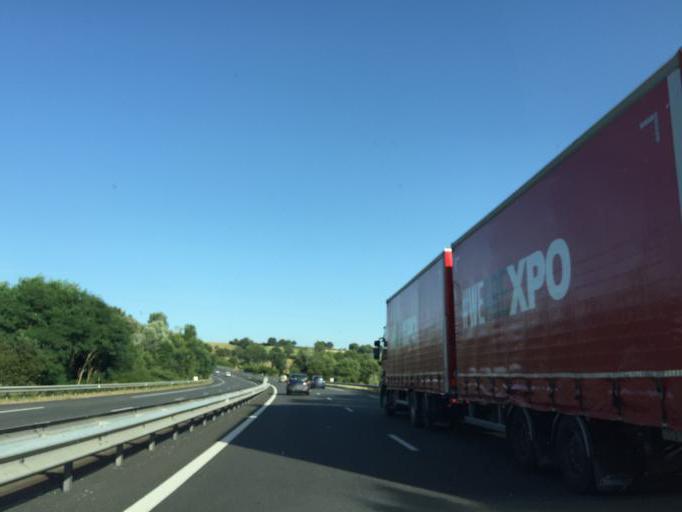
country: FR
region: Auvergne
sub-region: Departement de l'Allier
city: Montmarault
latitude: 46.3327
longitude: 2.8926
